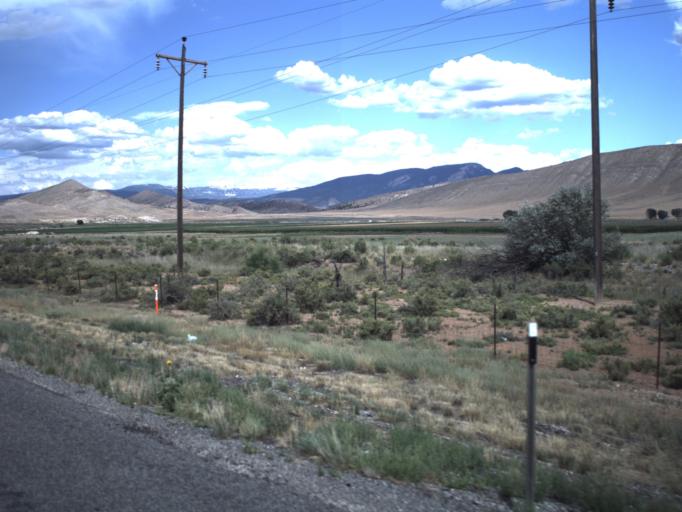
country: US
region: Utah
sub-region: Sevier County
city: Salina
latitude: 38.9931
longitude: -111.8458
